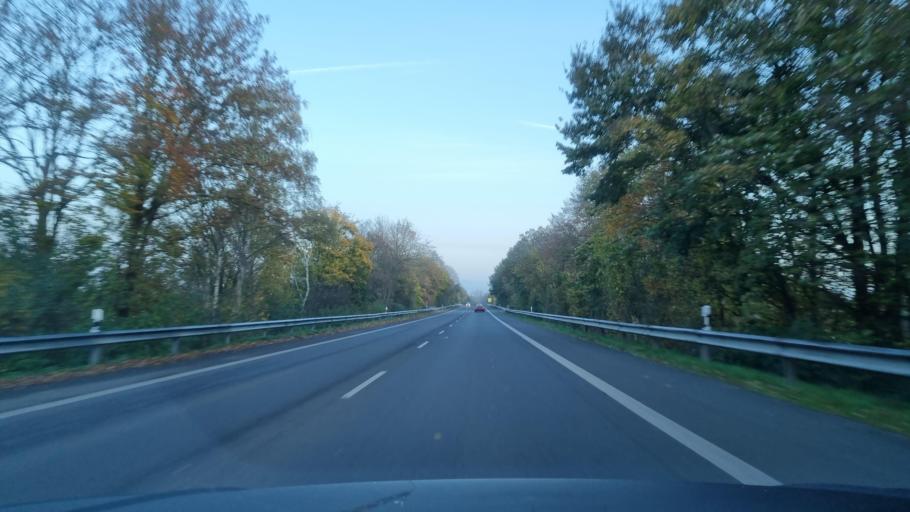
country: DE
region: North Rhine-Westphalia
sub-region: Regierungsbezirk Dusseldorf
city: Kranenburg
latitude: 51.7788
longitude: 6.0296
